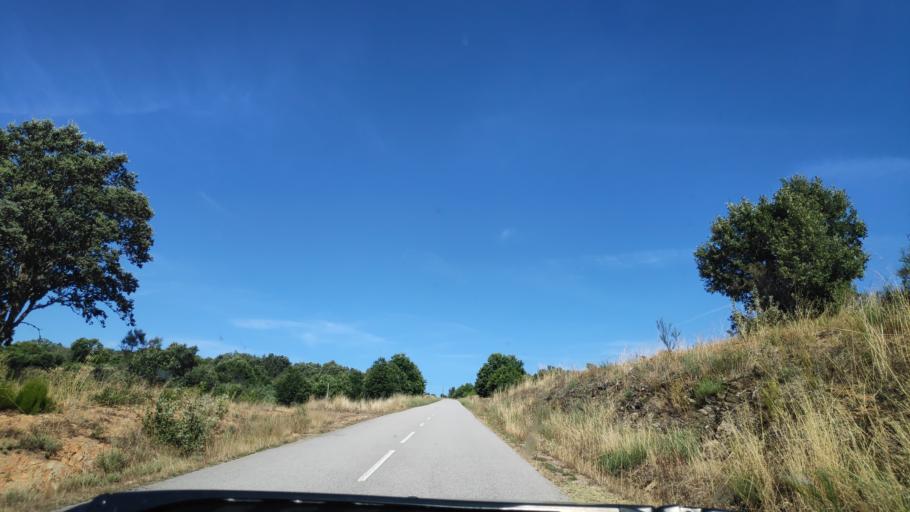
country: ES
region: Castille and Leon
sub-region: Provincia de Zamora
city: Alcanices
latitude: 41.6494
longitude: -6.3708
